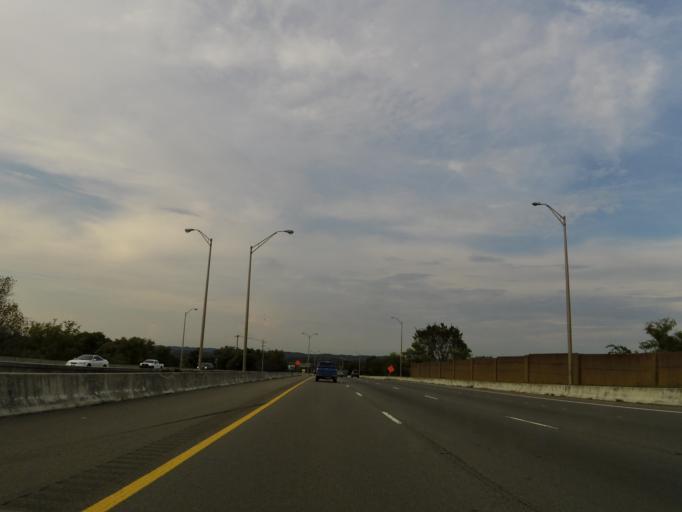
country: US
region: Tennessee
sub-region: Davidson County
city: Nashville
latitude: 36.1591
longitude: -86.8218
